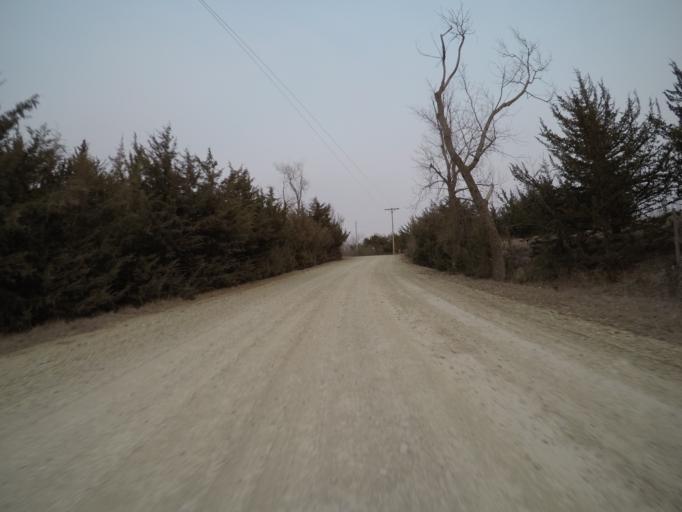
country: US
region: Kansas
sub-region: Riley County
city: Manhattan
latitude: 39.2452
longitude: -96.6546
